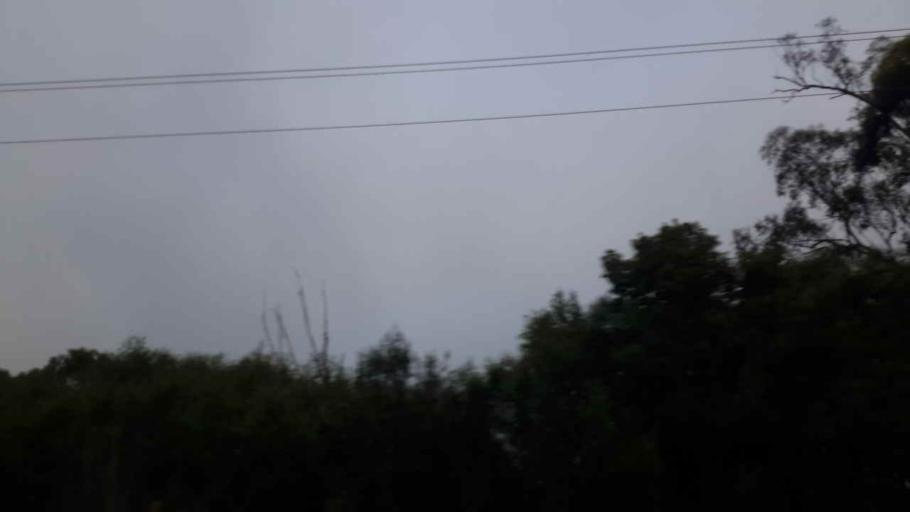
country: AU
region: New South Wales
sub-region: Camden
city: Camden South
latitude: -34.1009
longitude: 150.6956
